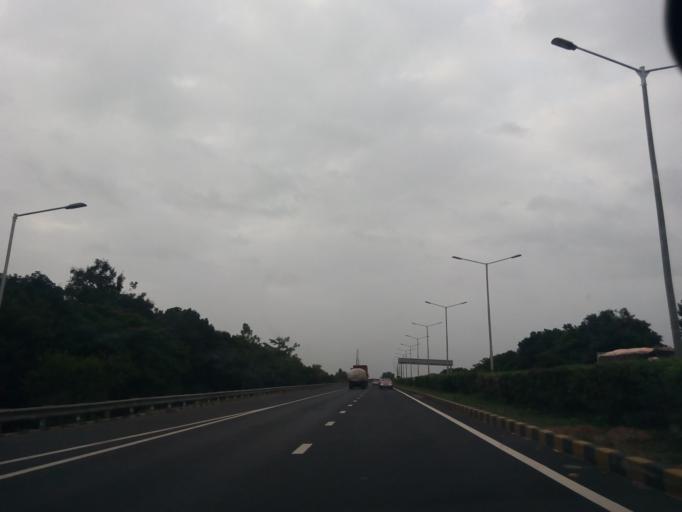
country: IN
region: Gujarat
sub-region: Kheda
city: Nadiad
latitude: 22.6936
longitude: 72.9002
